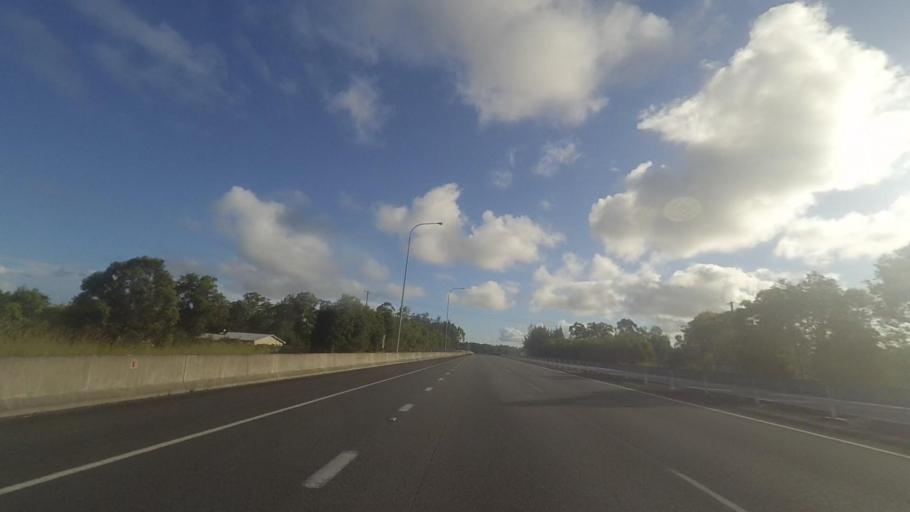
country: AU
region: New South Wales
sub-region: Great Lakes
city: Nabiac
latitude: -32.1030
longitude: 152.3748
